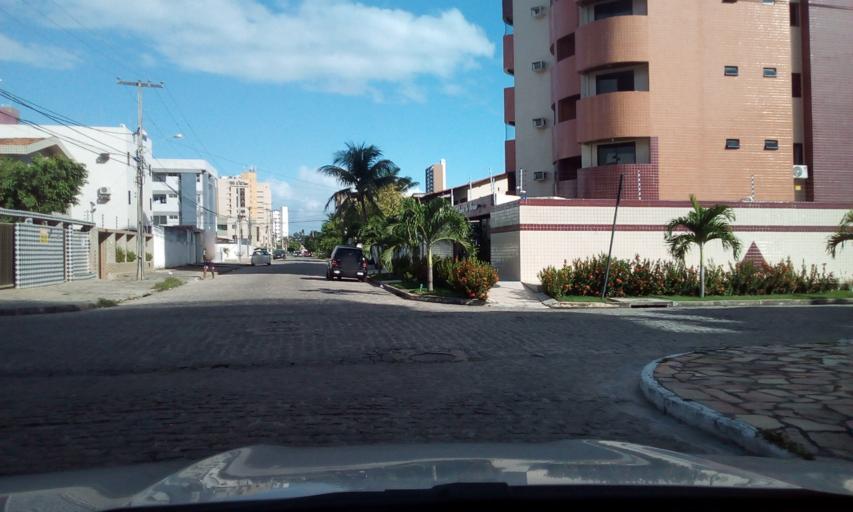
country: BR
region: Paraiba
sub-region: Joao Pessoa
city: Joao Pessoa
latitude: -7.0710
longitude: -34.8372
